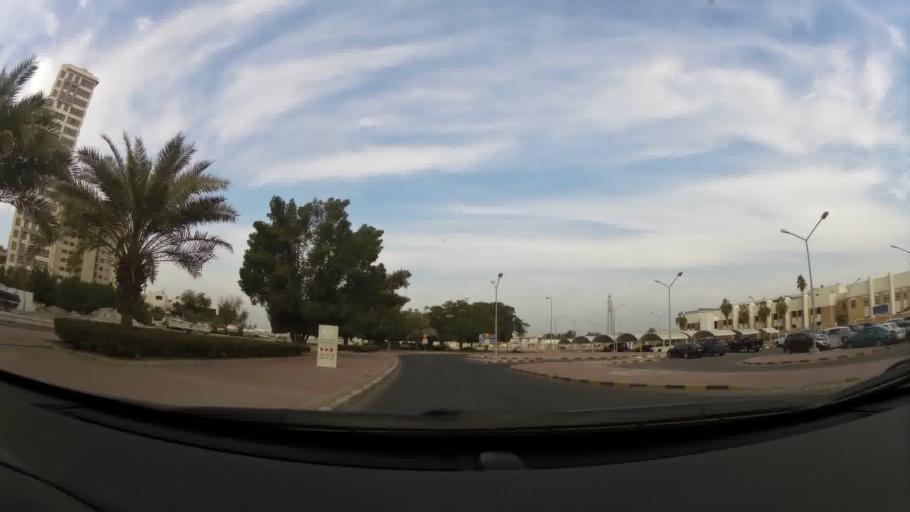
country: KW
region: Muhafazat Hawalli
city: As Salimiyah
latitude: 29.3477
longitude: 48.0971
